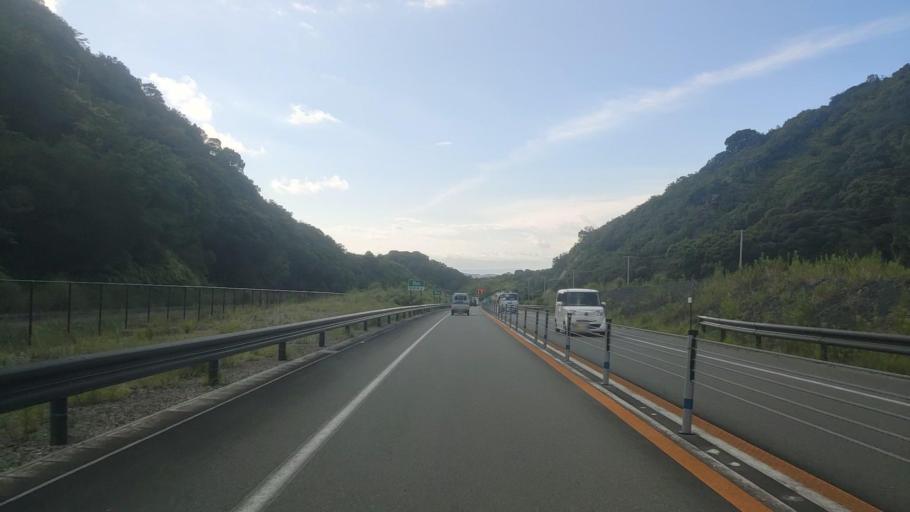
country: JP
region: Wakayama
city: Tanabe
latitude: 33.6344
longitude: 135.4117
